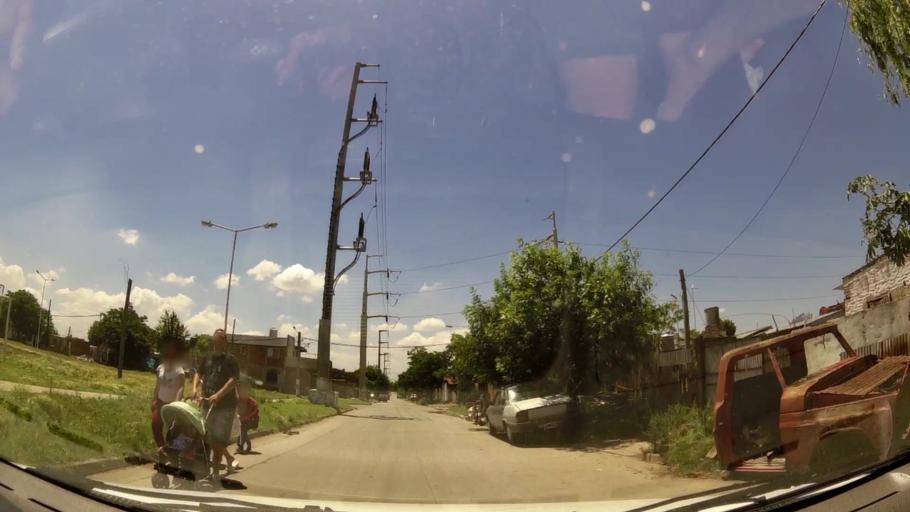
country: AR
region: Buenos Aires
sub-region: Partido de Merlo
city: Merlo
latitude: -34.6519
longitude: -58.7035
